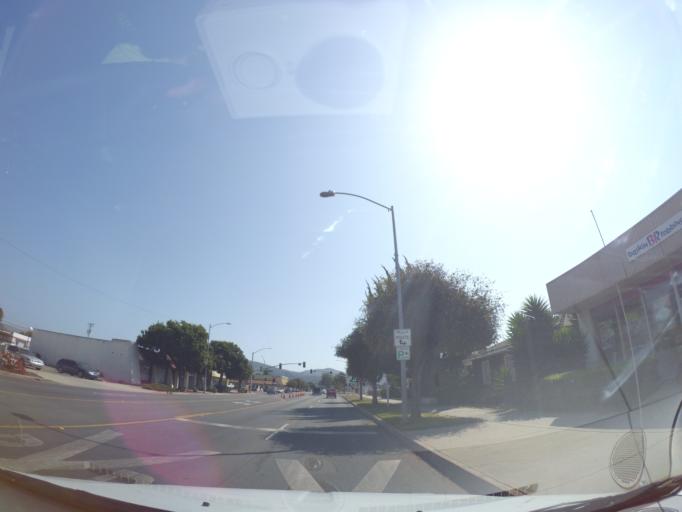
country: US
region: California
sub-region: Santa Barbara County
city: Lompoc
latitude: 34.6446
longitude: -120.4580
